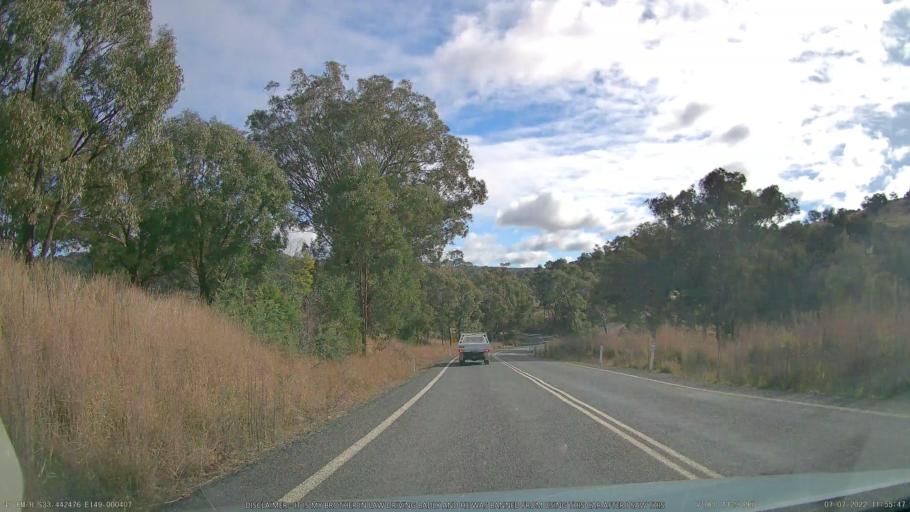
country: AU
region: New South Wales
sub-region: Blayney
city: Millthorpe
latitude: -33.4422
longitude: 149.0002
